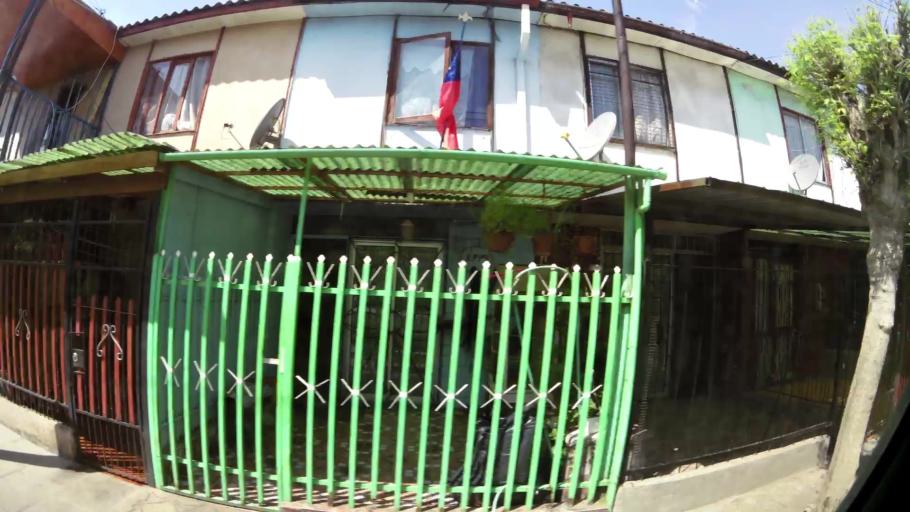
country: CL
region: Santiago Metropolitan
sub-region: Provincia de Santiago
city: Lo Prado
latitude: -33.4116
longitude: -70.7150
